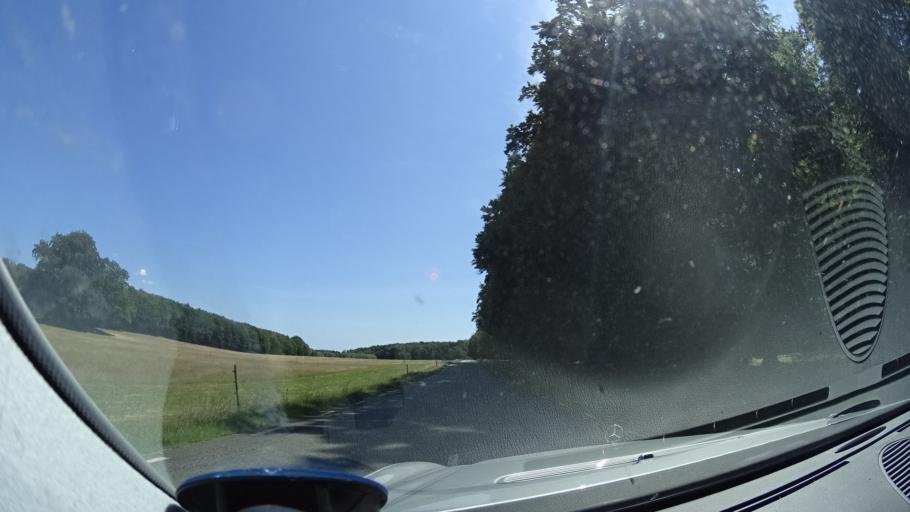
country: SE
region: Skane
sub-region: Kristianstads Kommun
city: Degeberga
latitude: 55.8985
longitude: 13.9978
